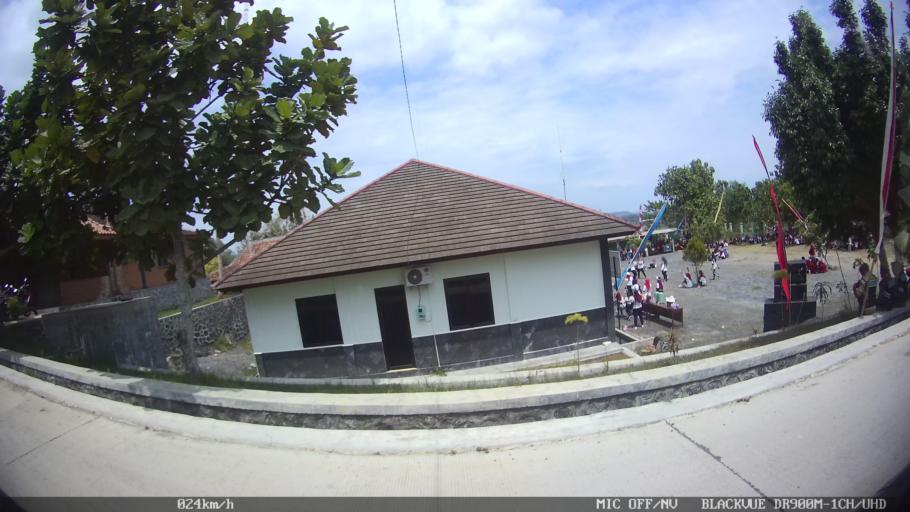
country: ID
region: Central Java
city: Candi Prambanan
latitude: -7.7836
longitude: 110.4938
